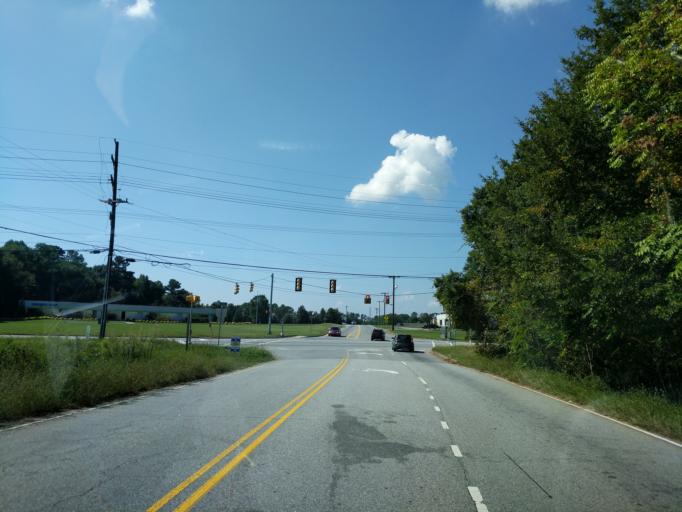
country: US
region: South Carolina
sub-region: Spartanburg County
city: Wellford
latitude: 34.8959
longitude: -82.0870
